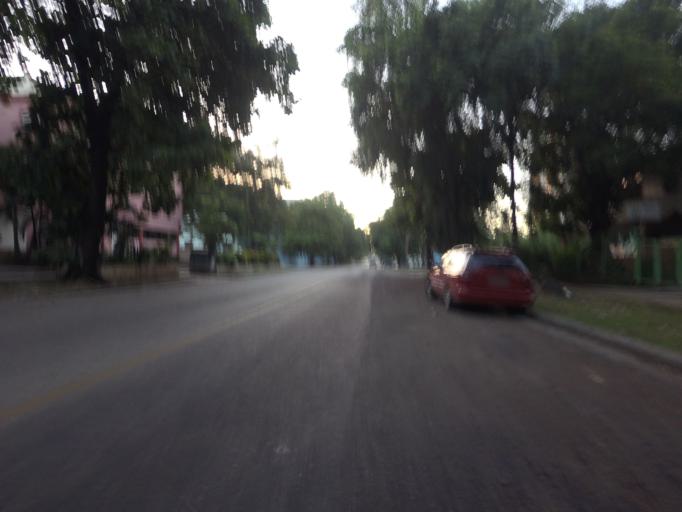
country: CU
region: La Habana
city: Cerro
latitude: 23.1161
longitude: -82.3933
